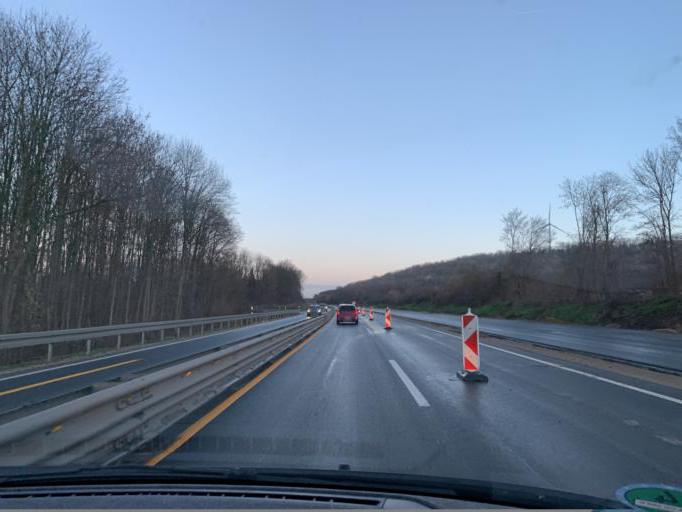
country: DE
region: North Rhine-Westphalia
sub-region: Regierungsbezirk Dusseldorf
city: Grevenbroich
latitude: 51.0759
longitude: 6.5940
